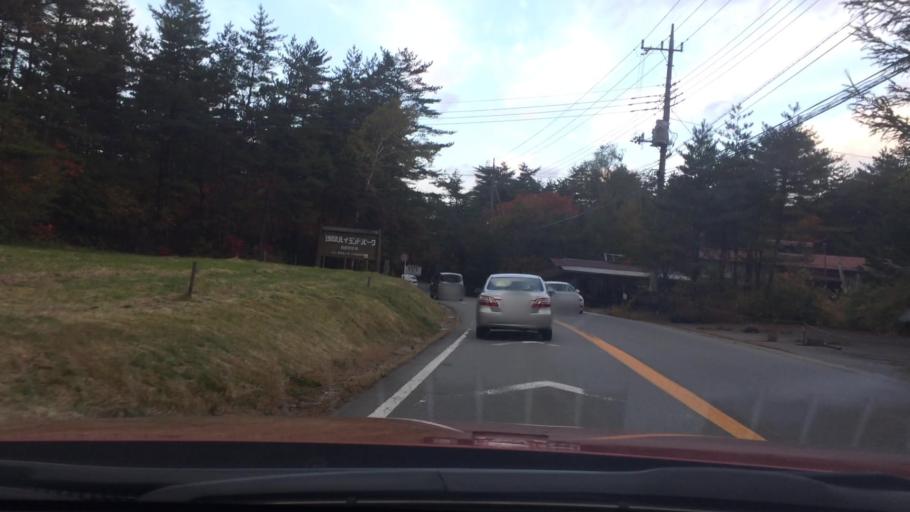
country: JP
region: Nagano
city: Komoro
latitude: 36.4300
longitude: 138.5716
